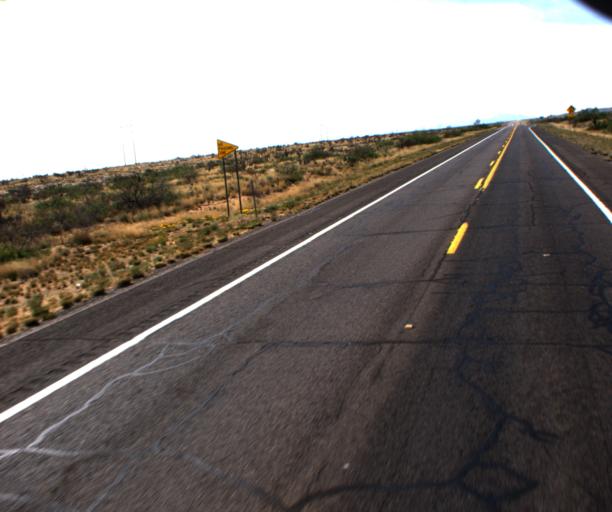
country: US
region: Arizona
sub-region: Graham County
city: Swift Trail Junction
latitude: 32.6017
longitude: -109.6860
